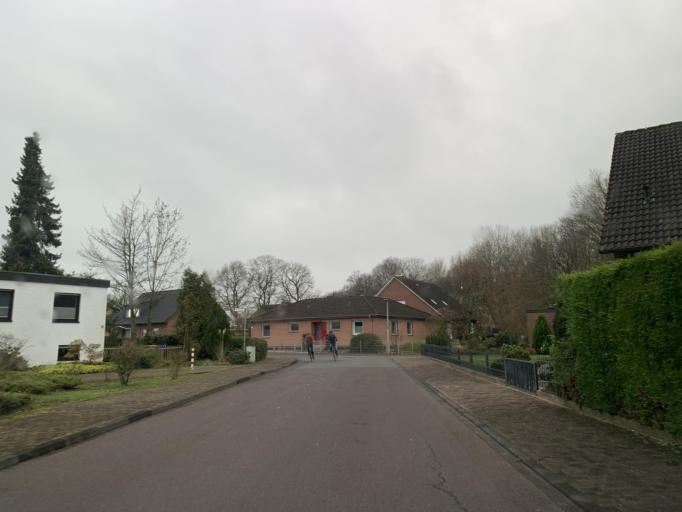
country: DE
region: North Rhine-Westphalia
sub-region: Regierungsbezirk Munster
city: Senden
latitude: 51.8587
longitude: 7.4701
